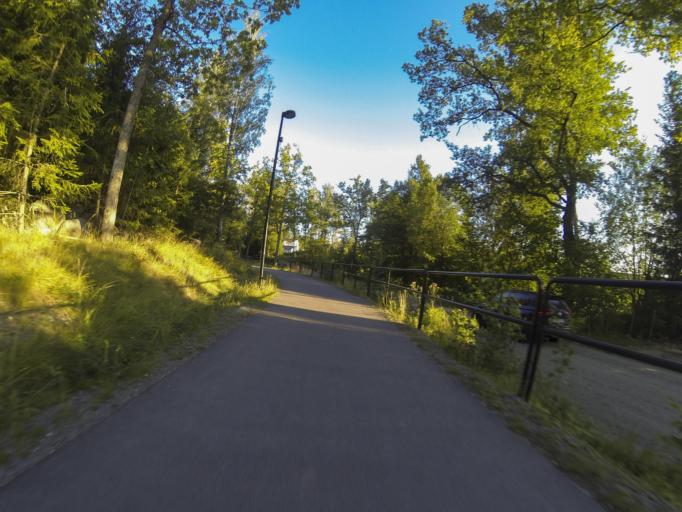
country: SE
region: Vaestmanland
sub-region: Vasteras
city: Vasteras
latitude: 59.5510
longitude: 16.6724
